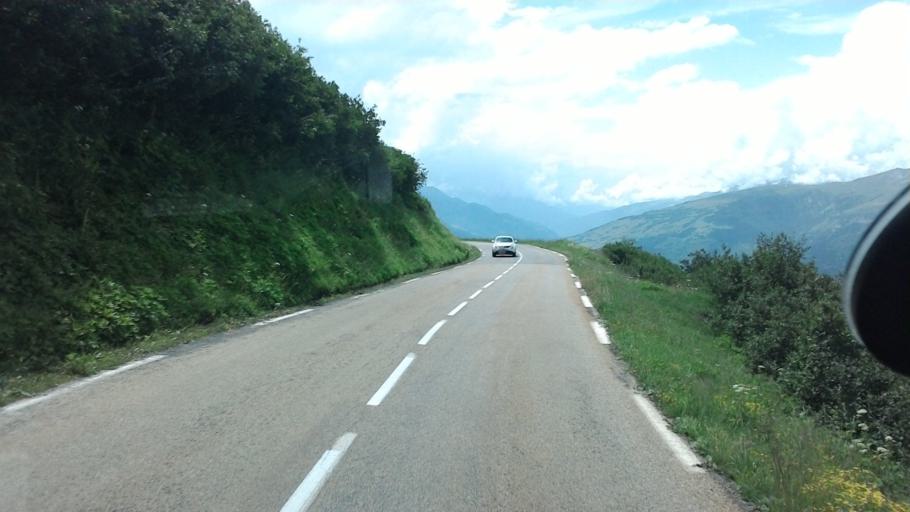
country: FR
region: Rhone-Alpes
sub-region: Departement de la Savoie
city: Seez
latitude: 45.6450
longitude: 6.8491
